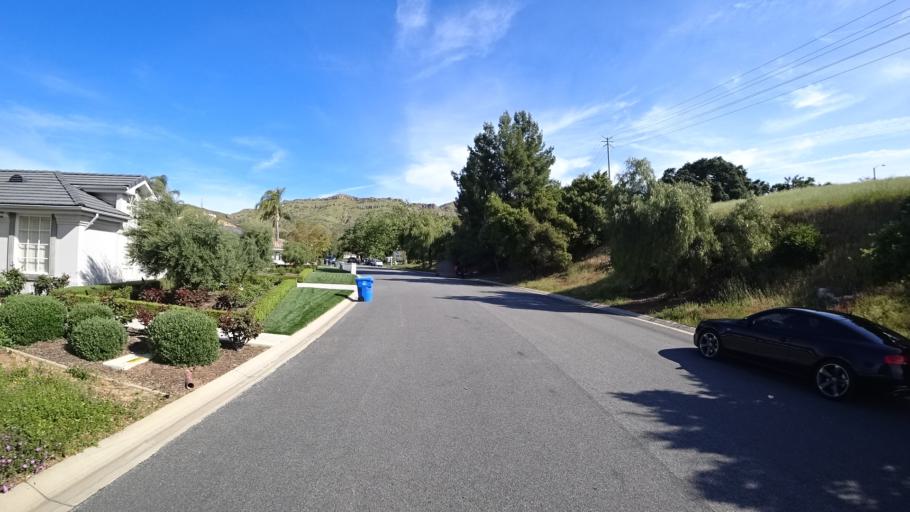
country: US
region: California
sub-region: Ventura County
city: Oak Park
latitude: 34.1888
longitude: -118.7858
